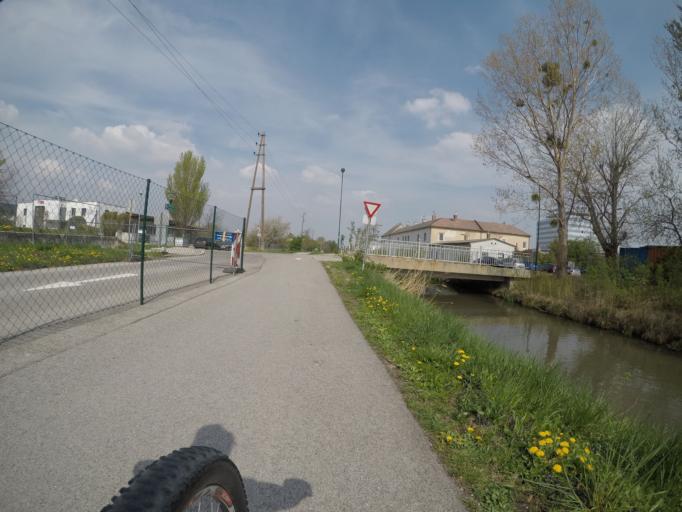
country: AT
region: Lower Austria
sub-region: Politischer Bezirk Modling
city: Gumpoldskirchen
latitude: 48.0355
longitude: 16.2907
